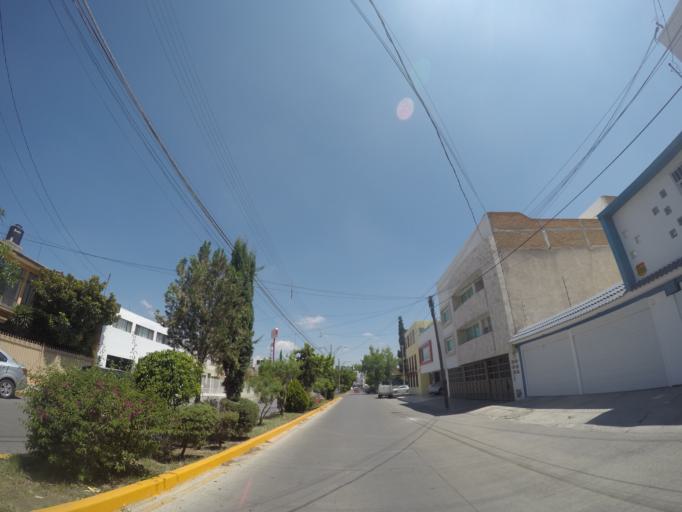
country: MX
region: San Luis Potosi
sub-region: San Luis Potosi
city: San Luis Potosi
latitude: 22.1460
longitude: -101.0017
